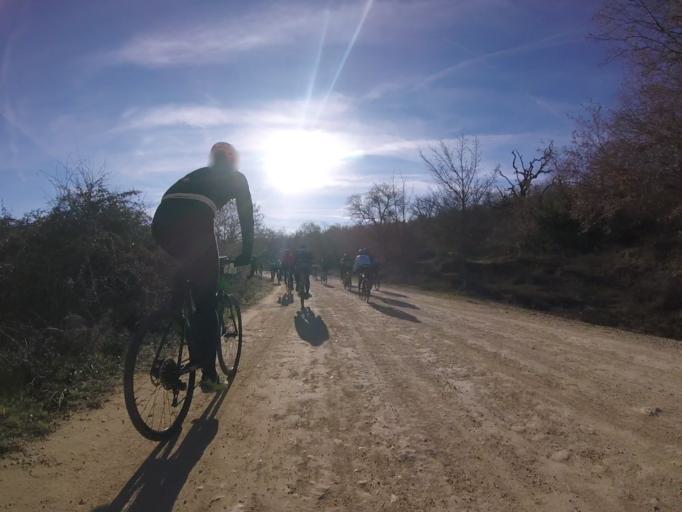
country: ES
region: Navarre
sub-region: Provincia de Navarra
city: Villatuerta
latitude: 42.6544
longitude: -1.9786
